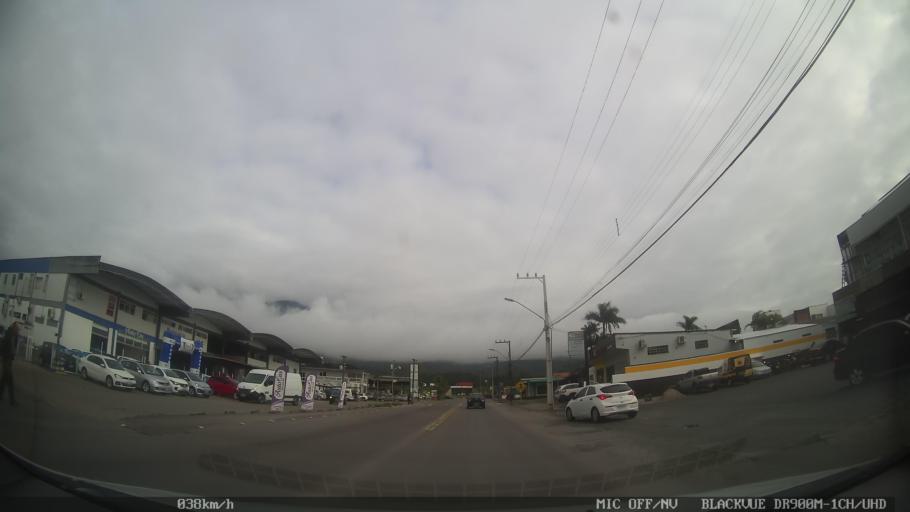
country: BR
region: Santa Catarina
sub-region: Joinville
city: Joinville
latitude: -26.0293
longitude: -48.8577
